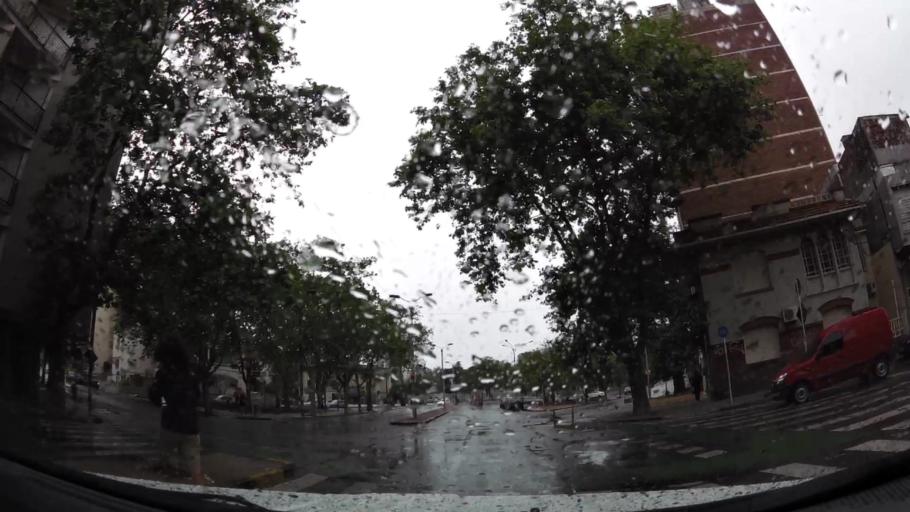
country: UY
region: Montevideo
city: Montevideo
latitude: -34.9106
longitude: -56.1661
